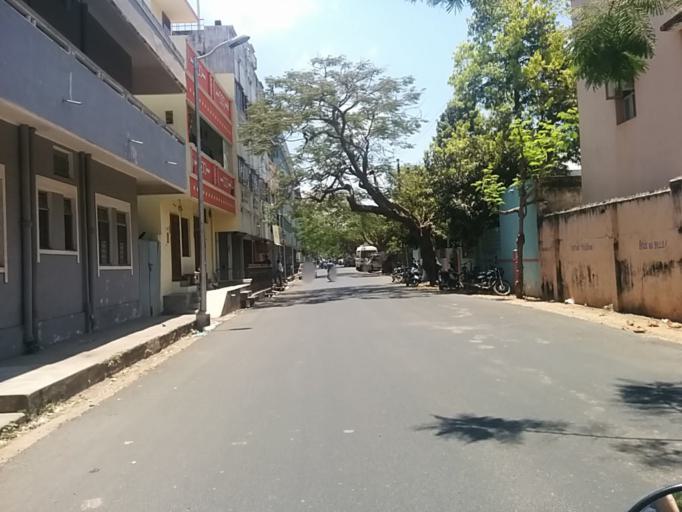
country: IN
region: Pondicherry
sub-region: Puducherry
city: Puducherry
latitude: 11.9388
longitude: 79.8335
